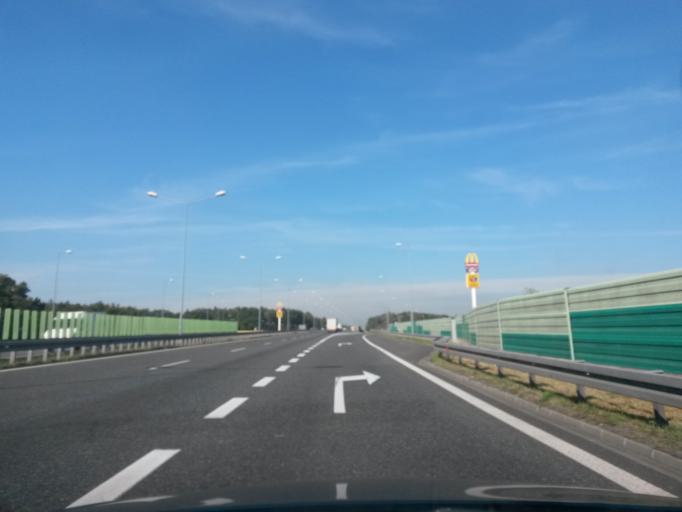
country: PL
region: Silesian Voivodeship
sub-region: Powiat gliwicki
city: Sosnicowice
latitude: 50.3079
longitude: 18.5521
